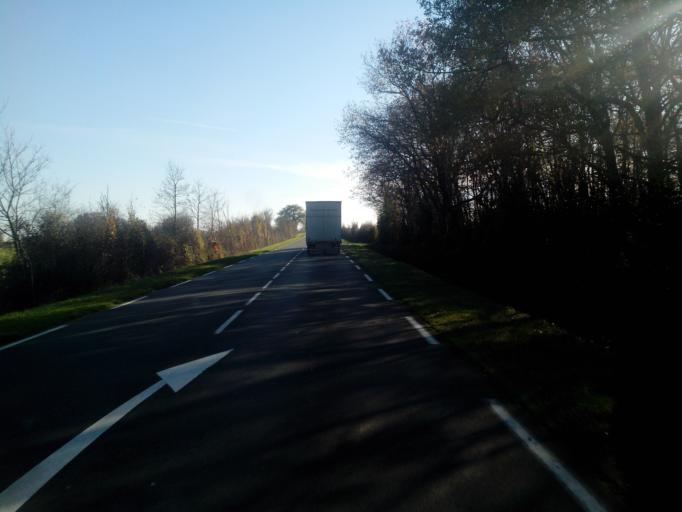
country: FR
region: Poitou-Charentes
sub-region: Departement de la Vienne
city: Lussac-les-Chateaux
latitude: 46.3896
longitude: 0.7400
